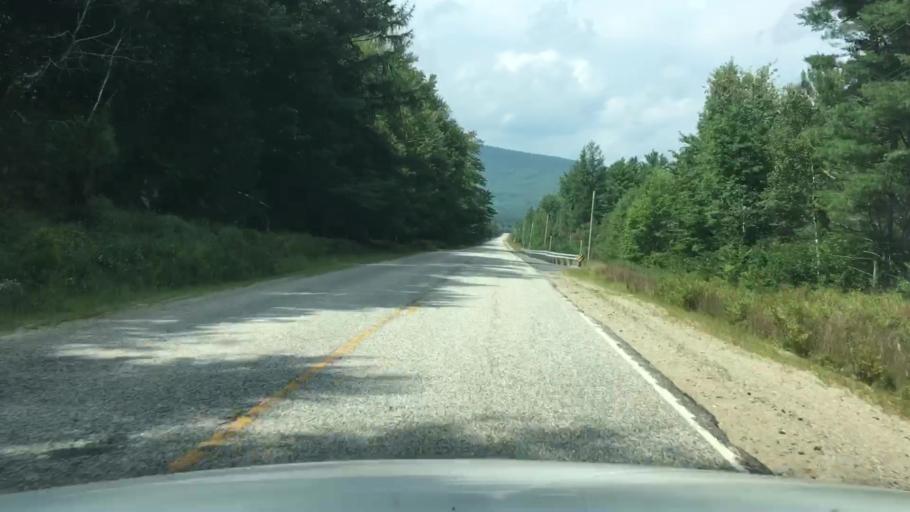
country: US
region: Maine
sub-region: Oxford County
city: Rumford
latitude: 44.5694
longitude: -70.7180
